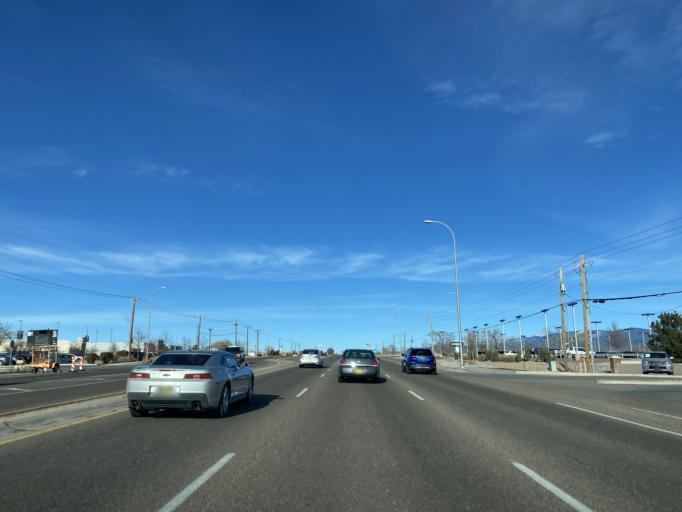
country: US
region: New Mexico
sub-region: Santa Fe County
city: Agua Fria
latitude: 35.6209
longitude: -106.0284
